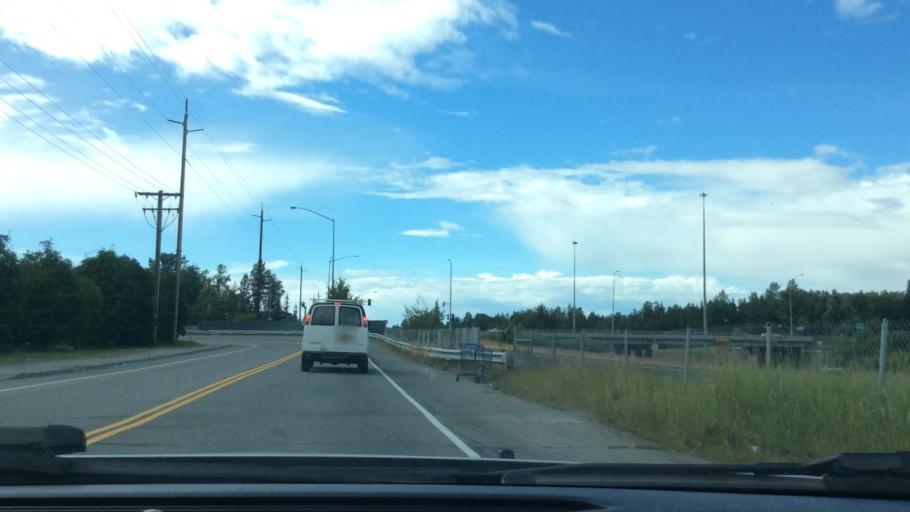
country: US
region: Alaska
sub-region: Anchorage Municipality
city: Anchorage
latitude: 61.2242
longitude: -149.7748
